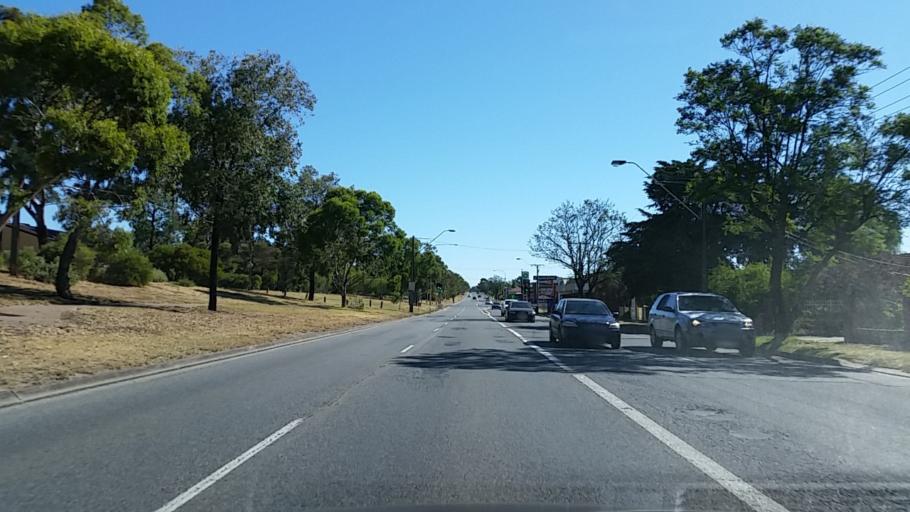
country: AU
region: South Australia
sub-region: Salisbury
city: Ingle Farm
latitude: -34.8267
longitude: 138.6335
